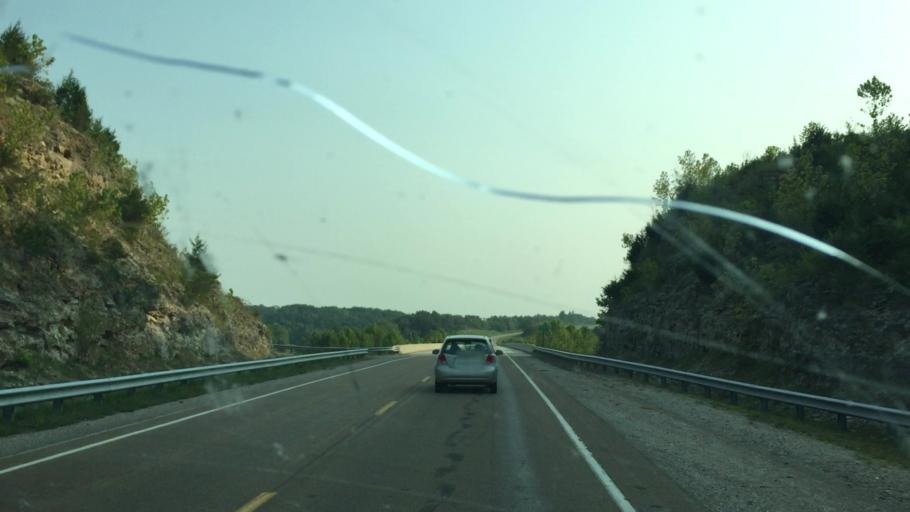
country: US
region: Missouri
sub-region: Pulaski County
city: Richland
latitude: 37.7995
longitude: -92.4056
